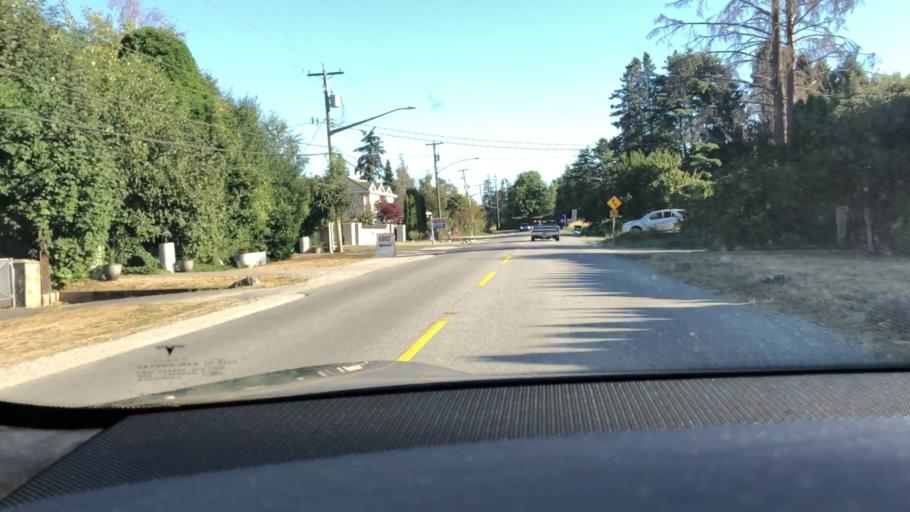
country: CA
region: British Columbia
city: Richmond
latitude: 49.1642
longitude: -123.0692
